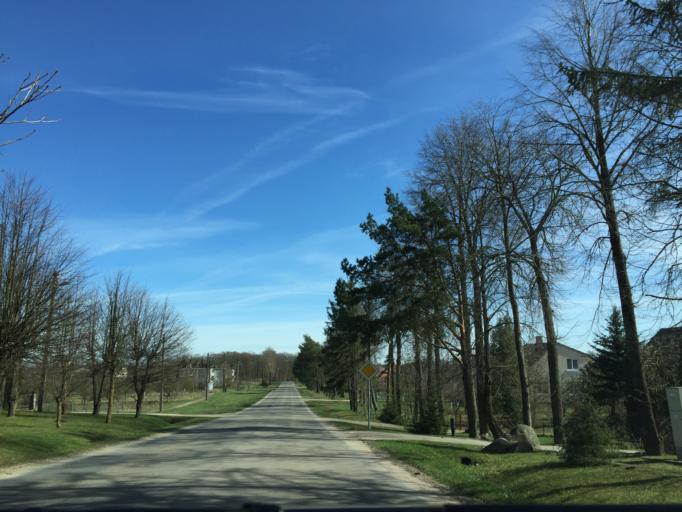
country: LT
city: Varniai
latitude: 55.7894
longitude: 22.6449
